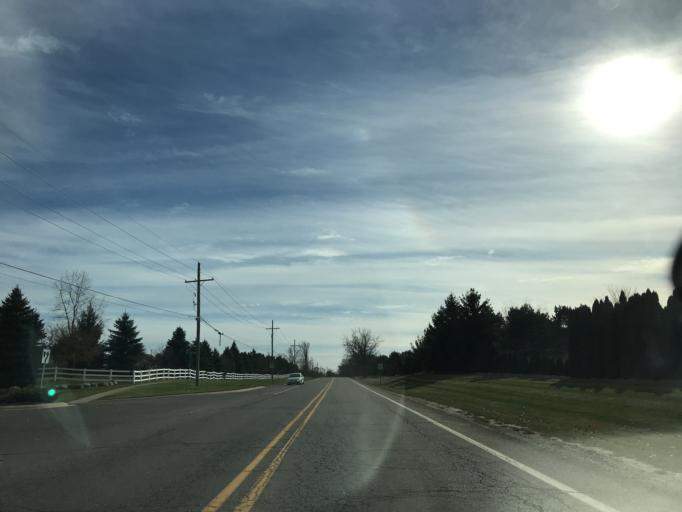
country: US
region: Michigan
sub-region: Oakland County
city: South Lyon
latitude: 42.4746
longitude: -83.6376
